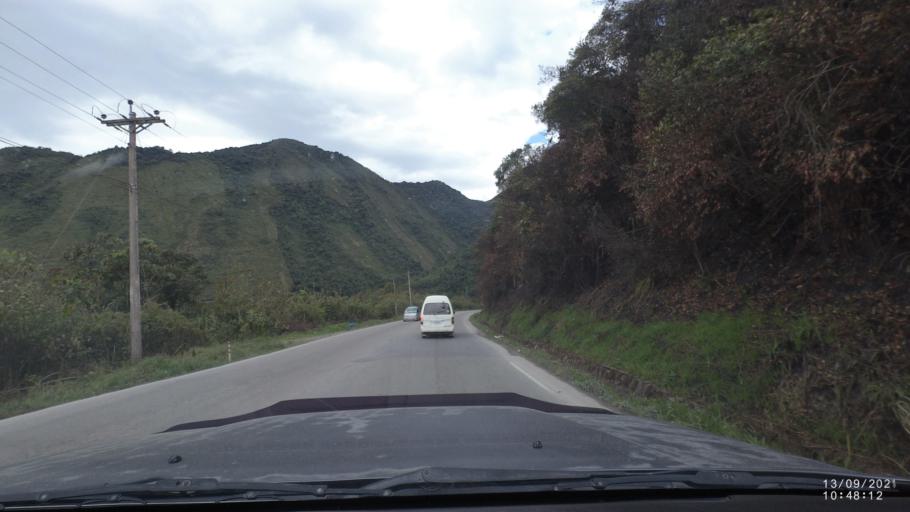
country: BO
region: Cochabamba
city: Colomi
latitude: -17.1999
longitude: -65.8614
